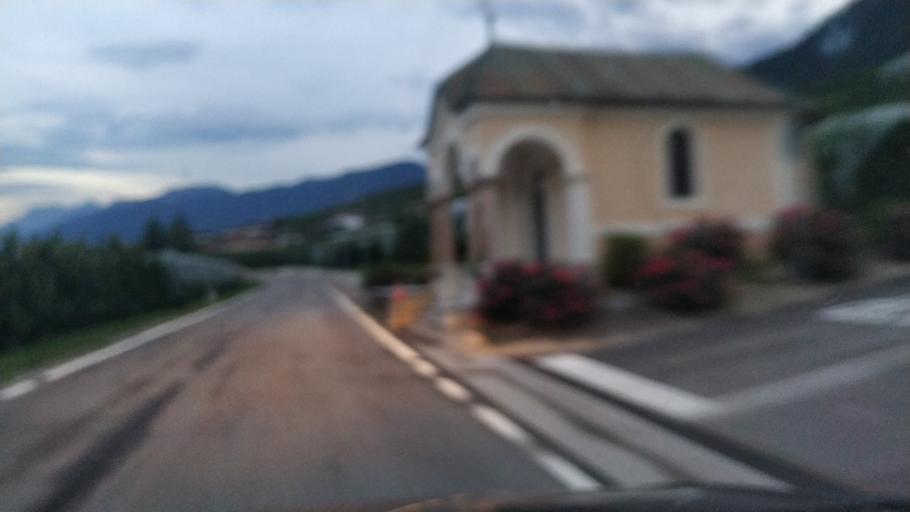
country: IT
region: Trentino-Alto Adige
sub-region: Provincia di Trento
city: Romallo
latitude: 46.4022
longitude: 11.0714
